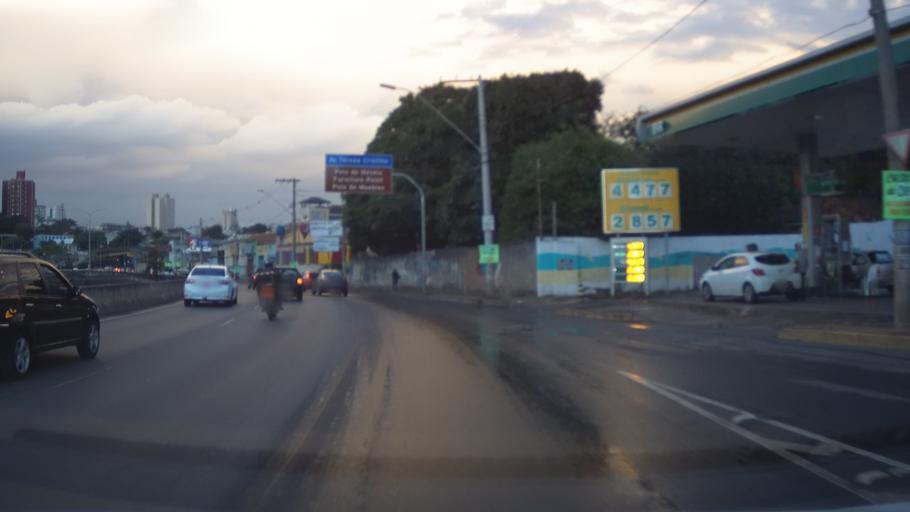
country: BR
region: Minas Gerais
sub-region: Belo Horizonte
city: Belo Horizonte
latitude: -19.9215
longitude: -43.9703
